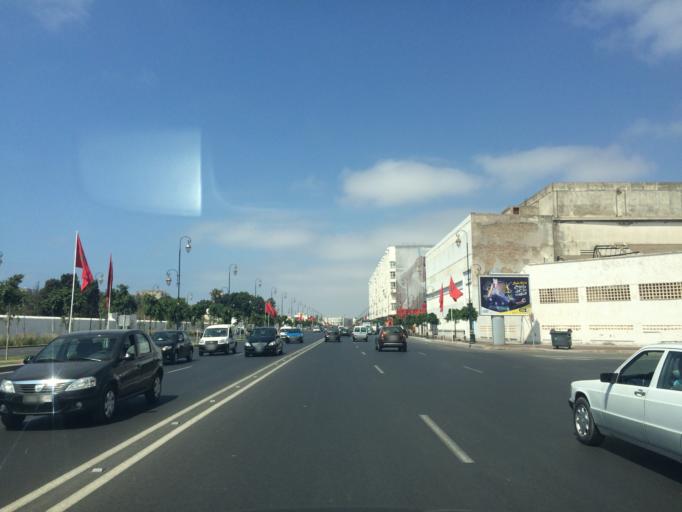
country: MA
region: Rabat-Sale-Zemmour-Zaer
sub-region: Rabat
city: Rabat
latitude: 34.0037
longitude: -6.8586
